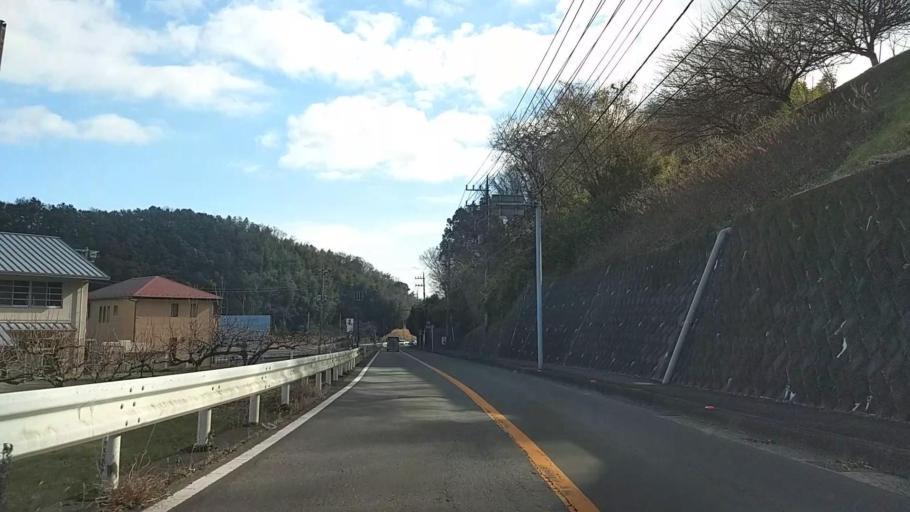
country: JP
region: Kanagawa
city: Isehara
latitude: 35.4381
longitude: 139.3019
